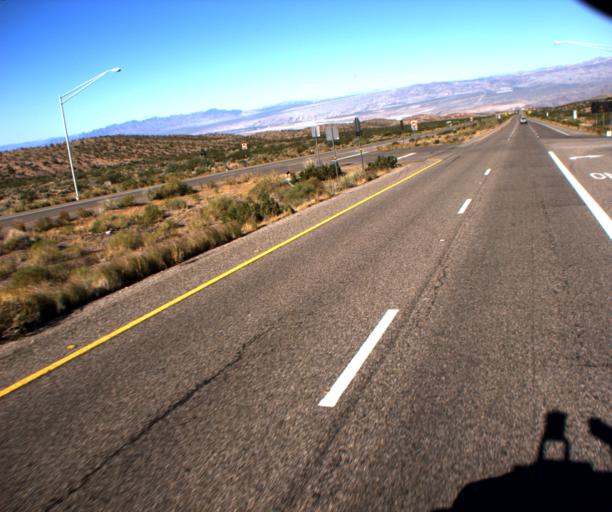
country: US
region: Nevada
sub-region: Clark County
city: Laughlin
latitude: 35.1857
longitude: -114.4577
